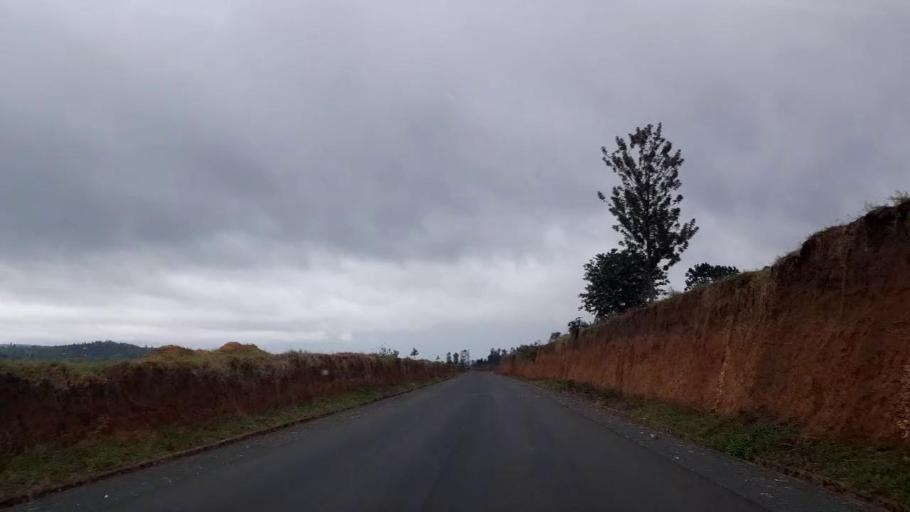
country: RW
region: Northern Province
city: Byumba
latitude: -1.4360
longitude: 30.2588
